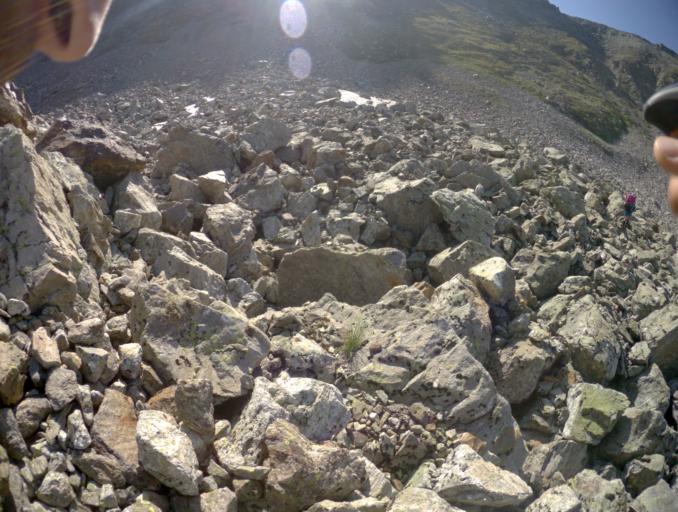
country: RU
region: Karachayevo-Cherkesiya
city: Uchkulan
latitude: 43.3083
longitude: 42.0663
